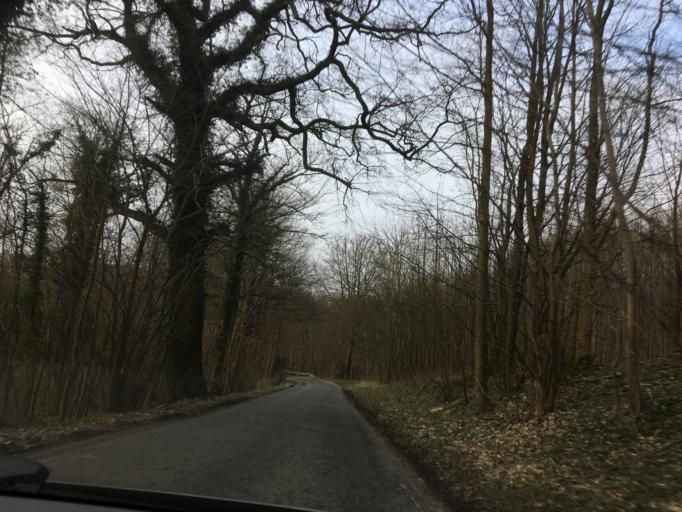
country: DK
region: South Denmark
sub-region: Vejle Kommune
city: Brejning
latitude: 55.7221
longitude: 9.6354
